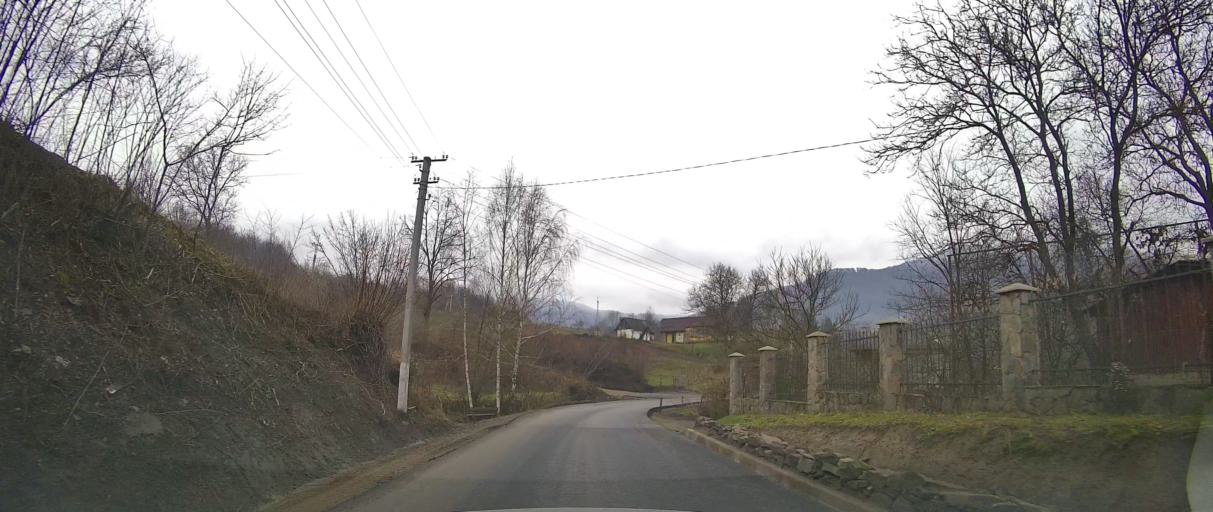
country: UA
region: Zakarpattia
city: Velykyi Bereznyi
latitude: 48.9642
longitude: 22.5486
